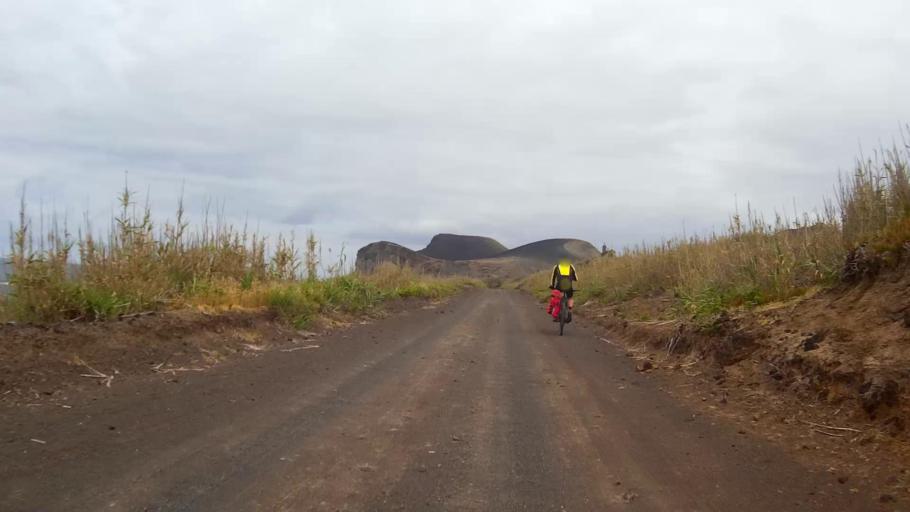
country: PT
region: Azores
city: Ribeira Grande
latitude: 38.5895
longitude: -28.8229
